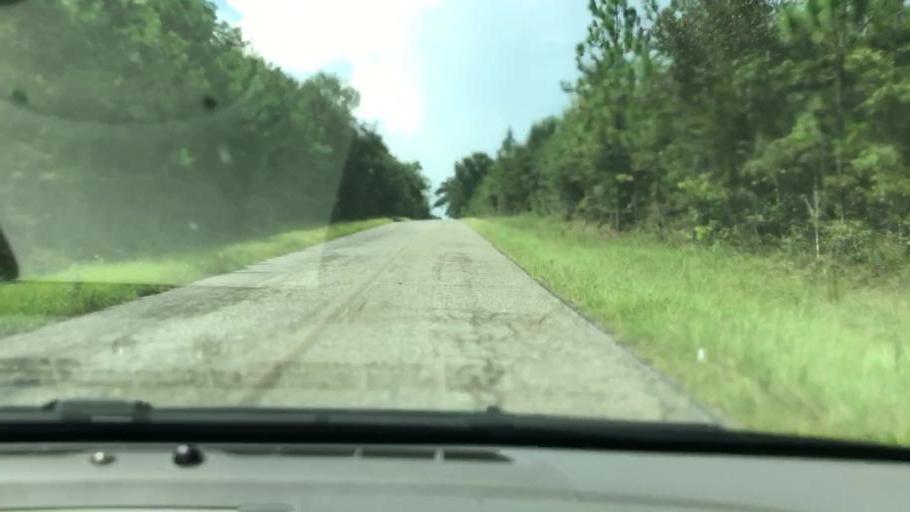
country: US
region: Georgia
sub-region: Seminole County
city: Donalsonville
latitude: 31.1618
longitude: -84.9977
